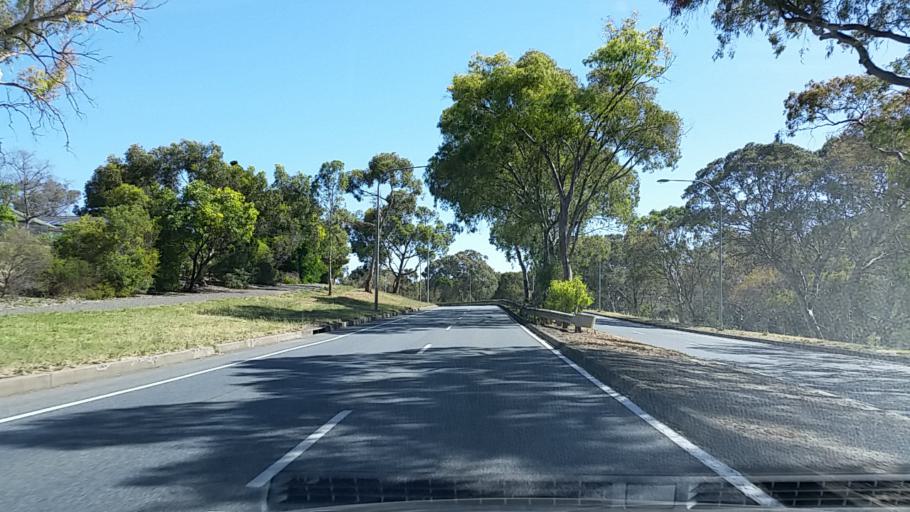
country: AU
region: South Australia
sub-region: Tea Tree Gully
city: Hope Valley
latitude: -34.8128
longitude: 138.6947
